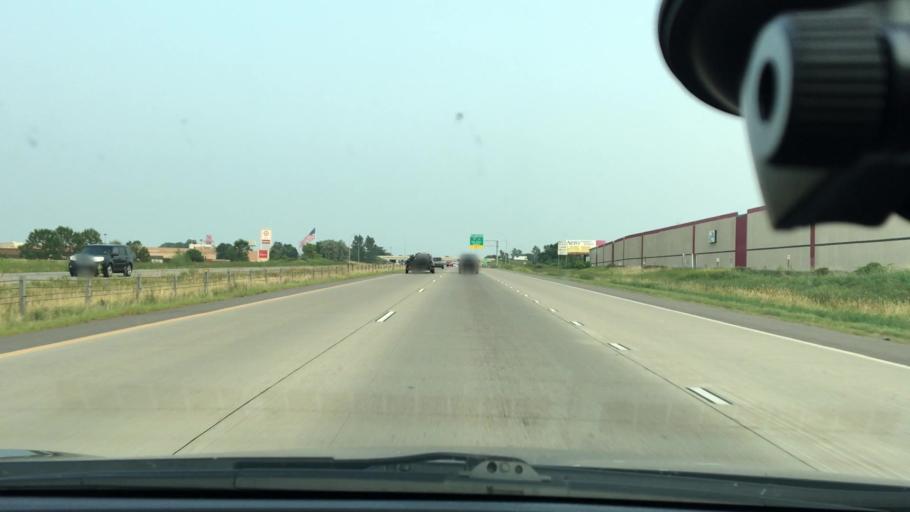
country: US
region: Minnesota
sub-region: Hennepin County
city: Rogers
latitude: 45.1979
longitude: -93.5600
